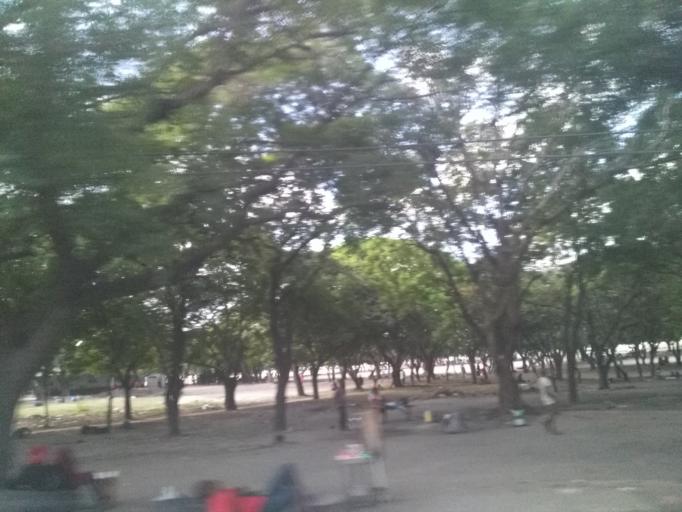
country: TZ
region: Dar es Salaam
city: Dar es Salaam
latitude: -6.8611
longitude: 39.2578
